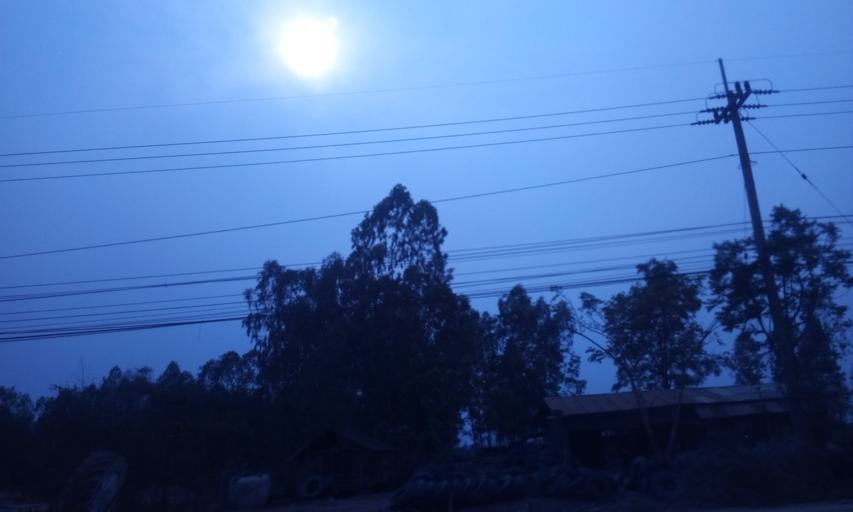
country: TH
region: Chachoengsao
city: Plaeng Yao
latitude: 13.5443
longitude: 101.2630
